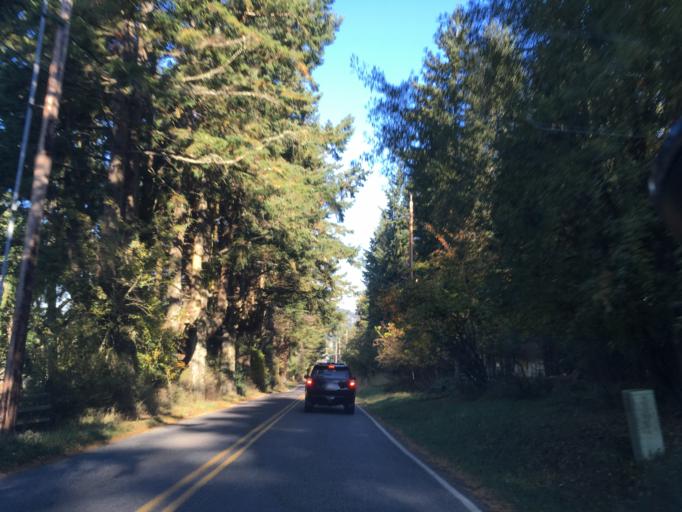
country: US
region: Washington
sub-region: San Juan County
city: Friday Harbor
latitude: 48.6677
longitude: -122.9282
